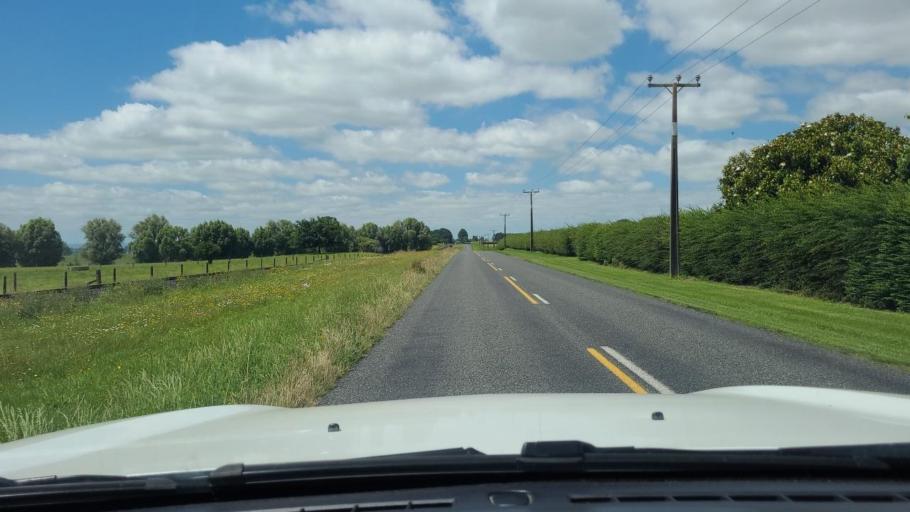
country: NZ
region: Waikato
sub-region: Matamata-Piako District
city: Matamata
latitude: -37.8685
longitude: 175.7558
